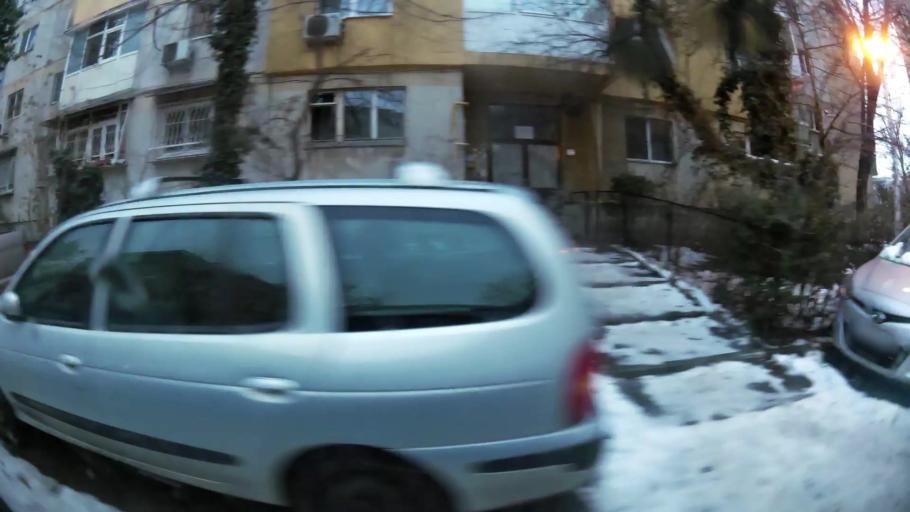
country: RO
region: Ilfov
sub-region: Comuna Chiajna
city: Rosu
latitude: 44.4313
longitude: 26.0213
